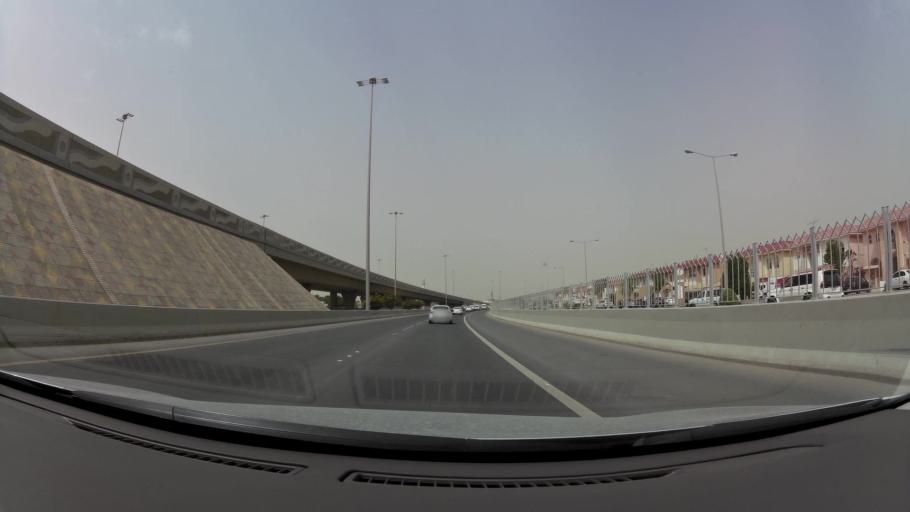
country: QA
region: Baladiyat ad Dawhah
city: Doha
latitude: 25.2547
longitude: 51.5082
